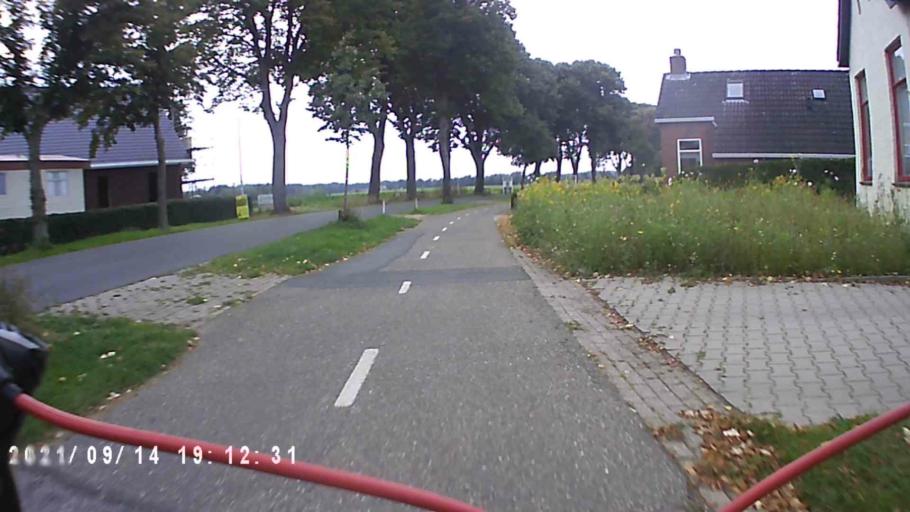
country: NL
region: Drenthe
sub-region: Gemeente Aa en Hunze
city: Anloo
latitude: 53.0634
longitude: 6.7121
